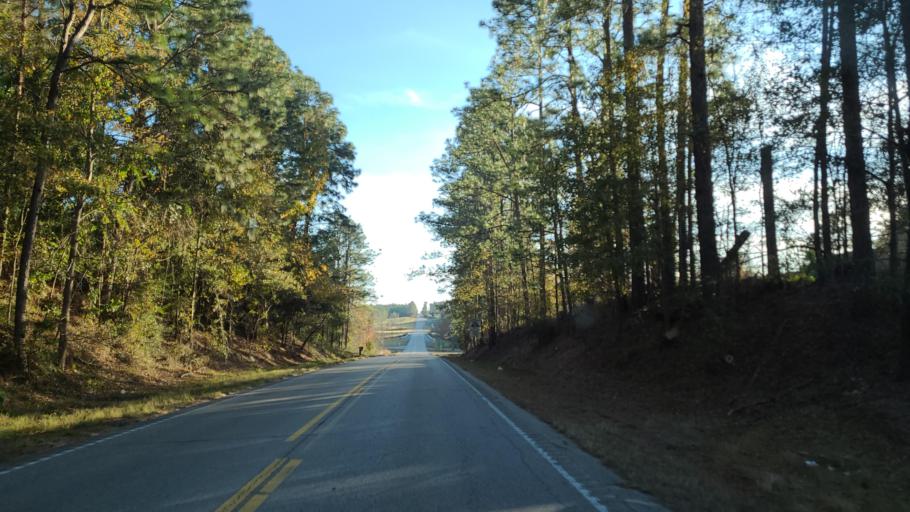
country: US
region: Mississippi
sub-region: Lamar County
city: Purvis
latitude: 31.1148
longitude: -89.4100
